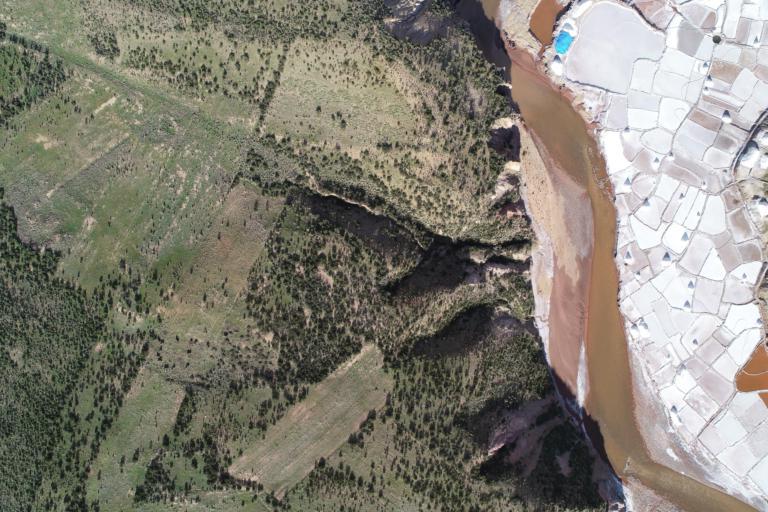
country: BO
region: La Paz
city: Patacamaya
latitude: -17.2987
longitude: -68.4877
